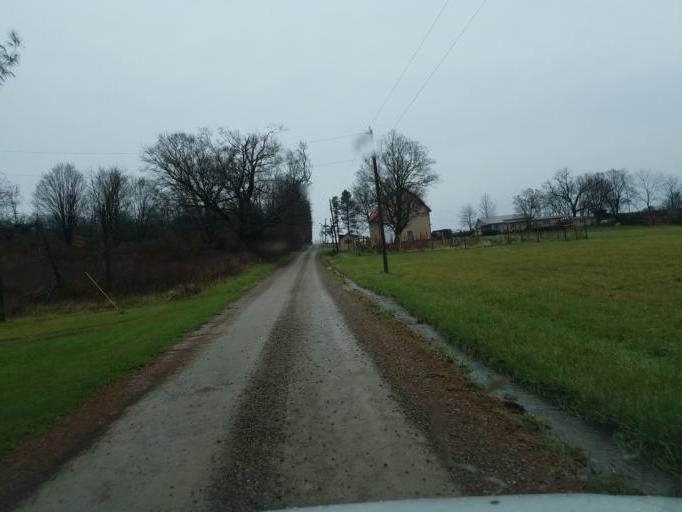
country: US
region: Ohio
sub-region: Knox County
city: Fredericktown
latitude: 40.4111
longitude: -82.6101
